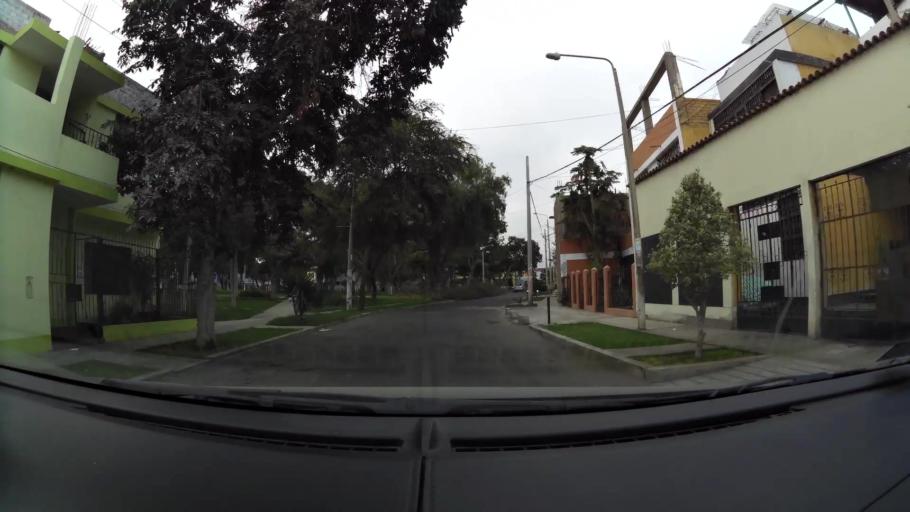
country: PE
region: La Libertad
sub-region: Provincia de Trujillo
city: Trujillo
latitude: -8.0999
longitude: -79.0301
